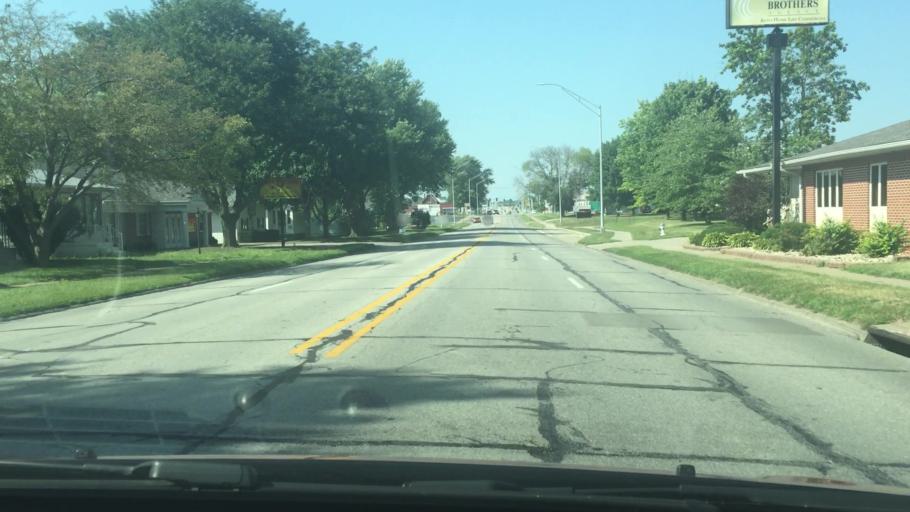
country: US
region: Iowa
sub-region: Muscatine County
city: Muscatine
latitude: 41.4387
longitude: -91.0307
